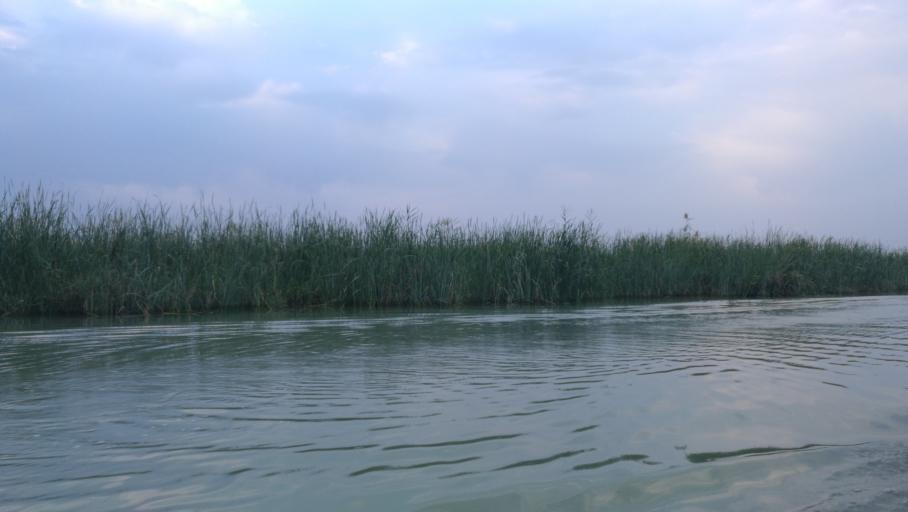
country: IQ
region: Dhi Qar
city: Al Jabayish
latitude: 30.9796
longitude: 47.0413
